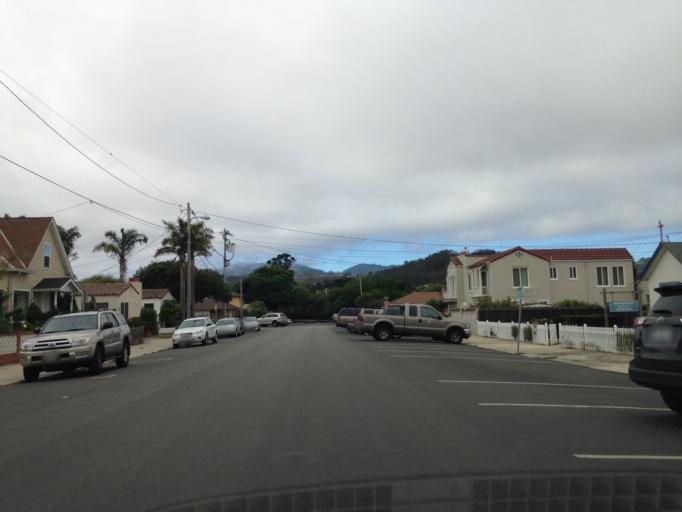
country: US
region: California
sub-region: San Mateo County
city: Half Moon Bay
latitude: 37.4638
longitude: -122.4283
